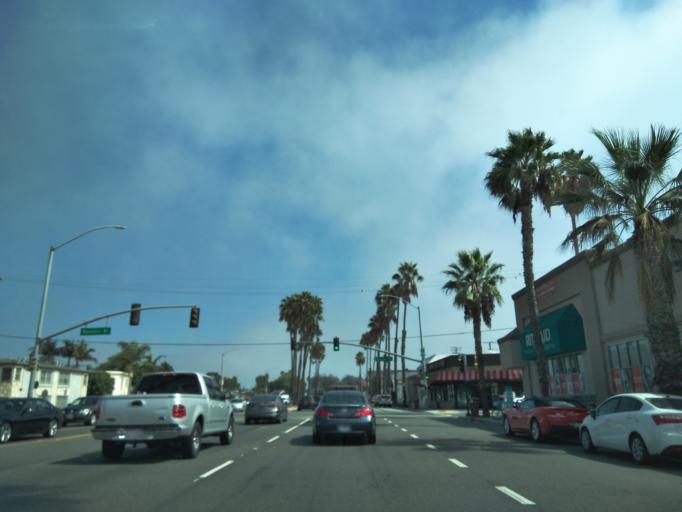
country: US
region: California
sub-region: Orange County
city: Seal Beach
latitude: 33.7569
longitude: -118.1235
